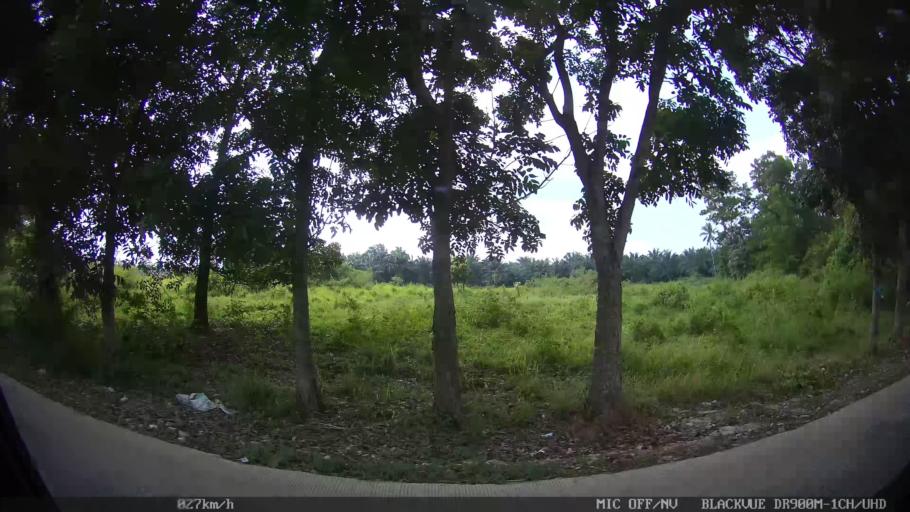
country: ID
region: Lampung
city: Kedaton
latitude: -5.3335
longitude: 105.2798
